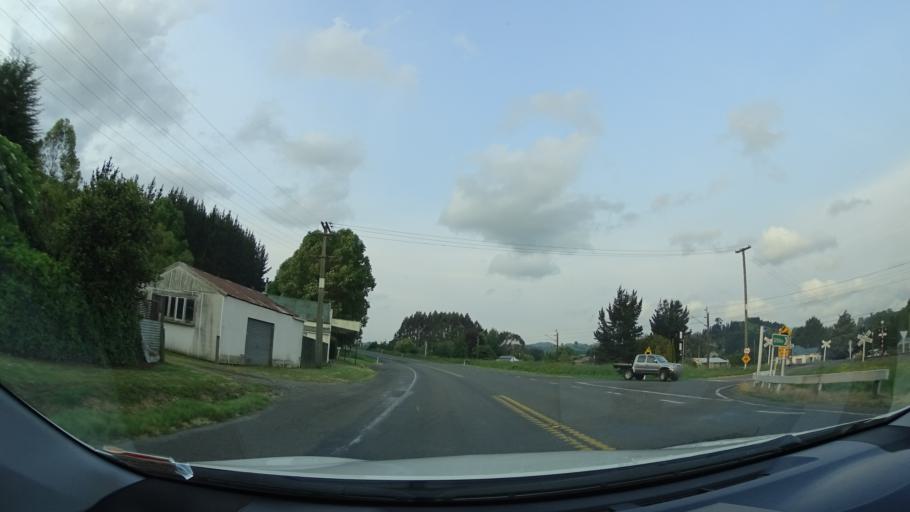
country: NZ
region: Manawatu-Wanganui
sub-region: Ruapehu District
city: Waiouru
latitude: -39.7335
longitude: 175.8436
